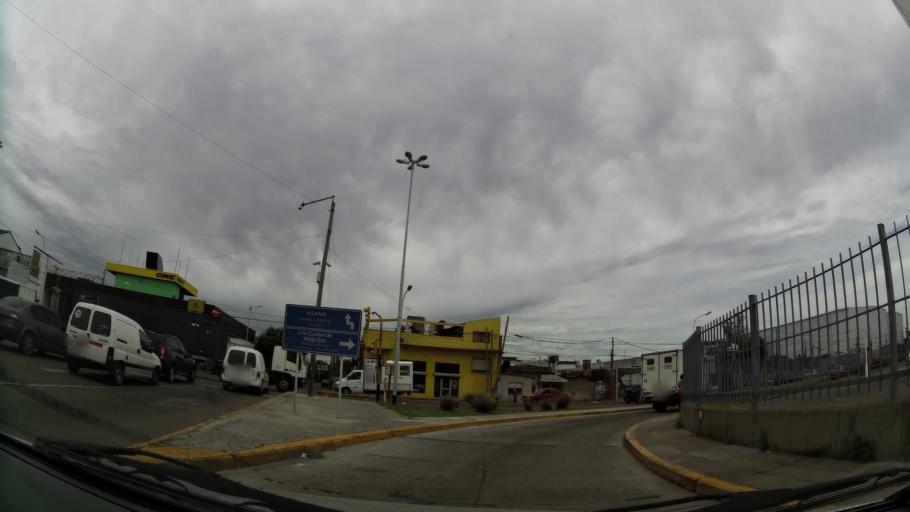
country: AR
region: Buenos Aires
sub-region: Partido de Avellaneda
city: Avellaneda
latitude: -34.6784
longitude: -58.3683
